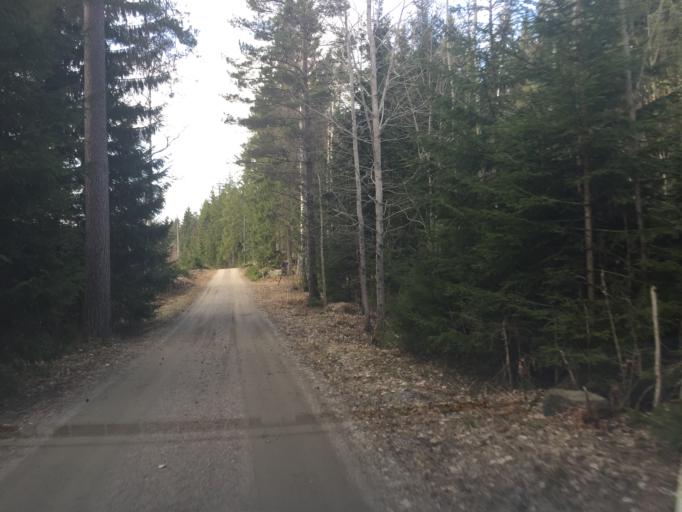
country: SE
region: Soedermanland
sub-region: Vingakers Kommun
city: Vingaker
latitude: 58.9916
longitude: 15.6868
